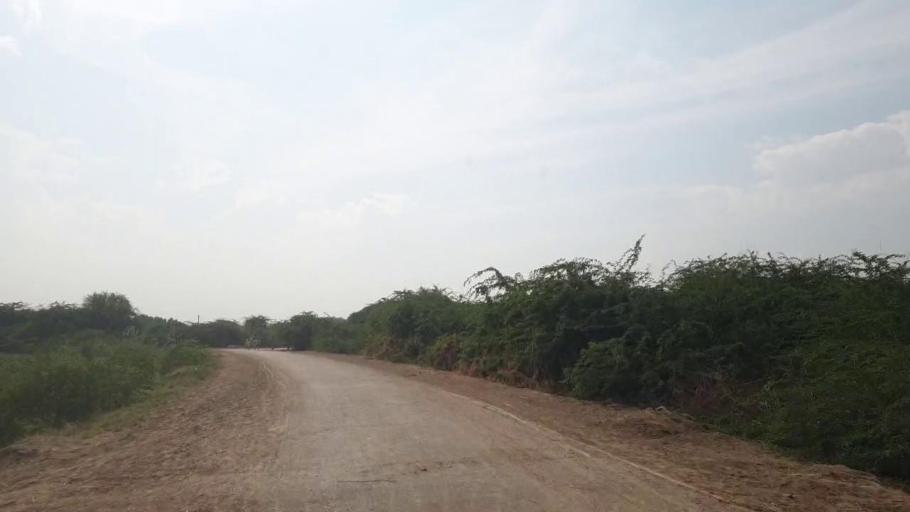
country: PK
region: Sindh
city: Rajo Khanani
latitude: 24.9626
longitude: 69.0112
